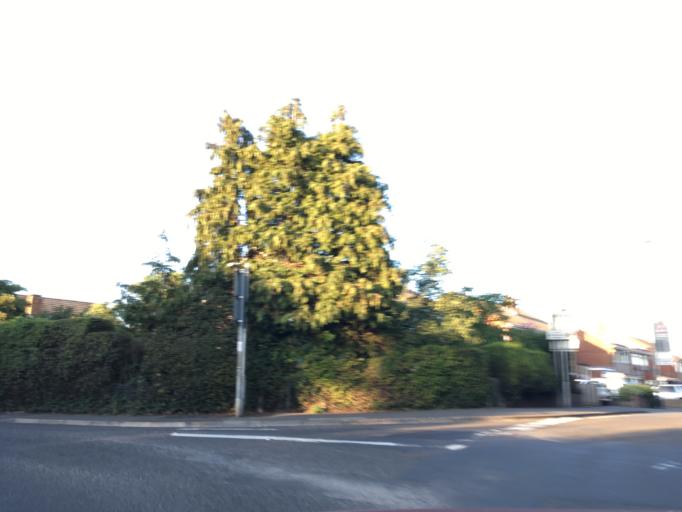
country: GB
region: England
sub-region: Bath and North East Somerset
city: Whitchurch
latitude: 51.4089
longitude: -2.5478
